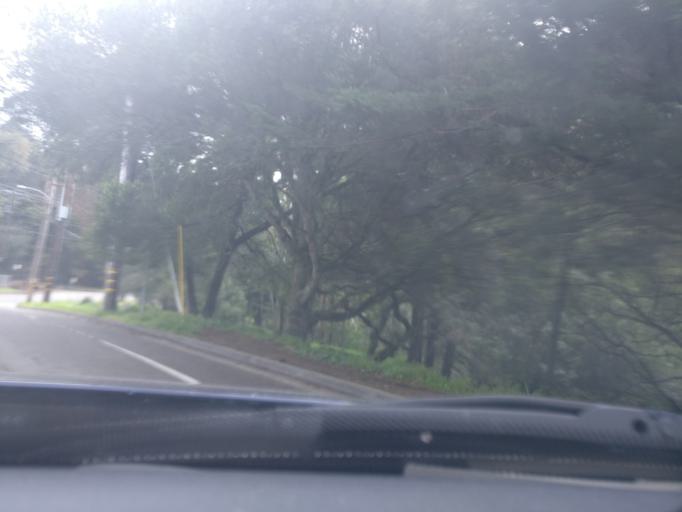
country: US
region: California
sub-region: Alameda County
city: Piedmont
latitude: 37.8189
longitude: -122.2063
